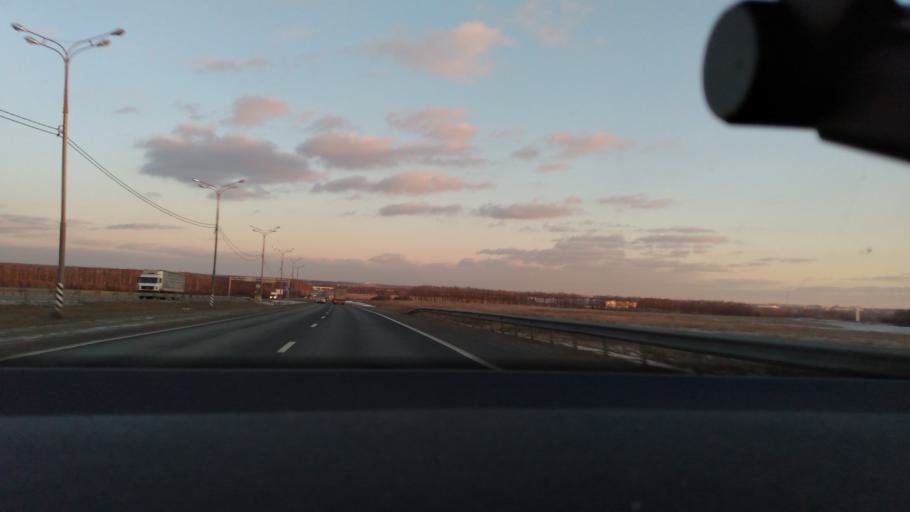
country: RU
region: Moskovskaya
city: Raduzhnyy
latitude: 55.1532
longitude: 38.6986
